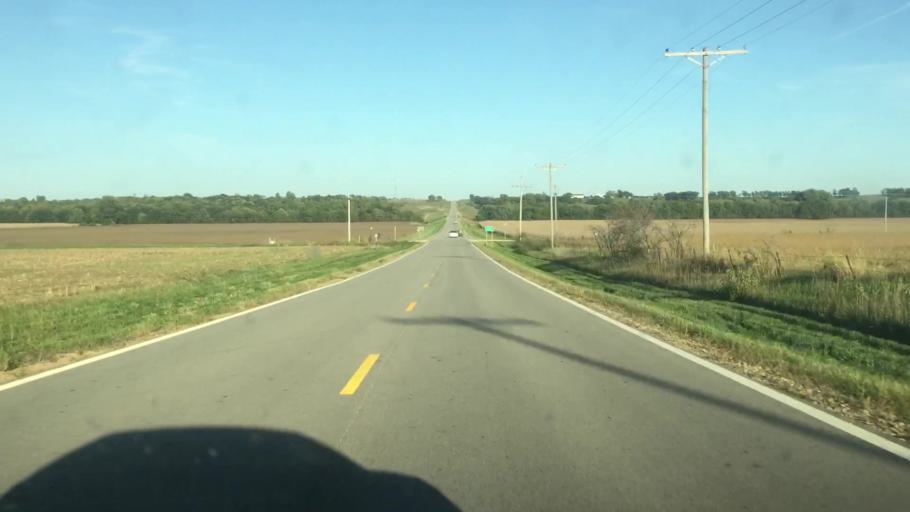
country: US
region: Kansas
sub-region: Brown County
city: Horton
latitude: 39.5875
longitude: -95.5659
